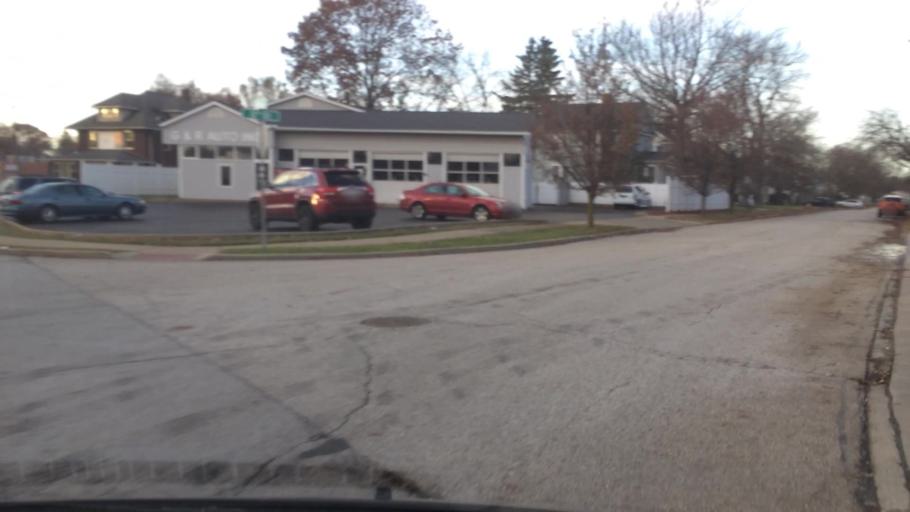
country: US
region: Ohio
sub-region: Summit County
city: Cuyahoga Falls
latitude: 41.1403
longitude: -81.4930
